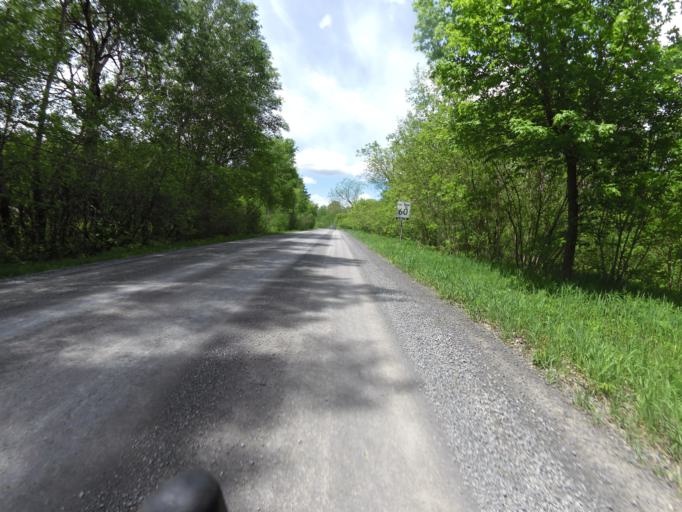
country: CA
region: Ontario
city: Ottawa
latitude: 45.3935
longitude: -75.5291
